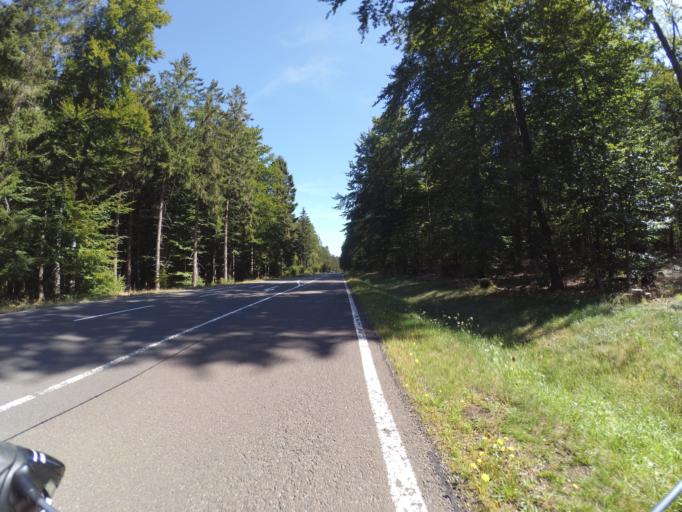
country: DE
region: Rheinland-Pfalz
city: Deuselbach
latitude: 49.7407
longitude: 7.0803
